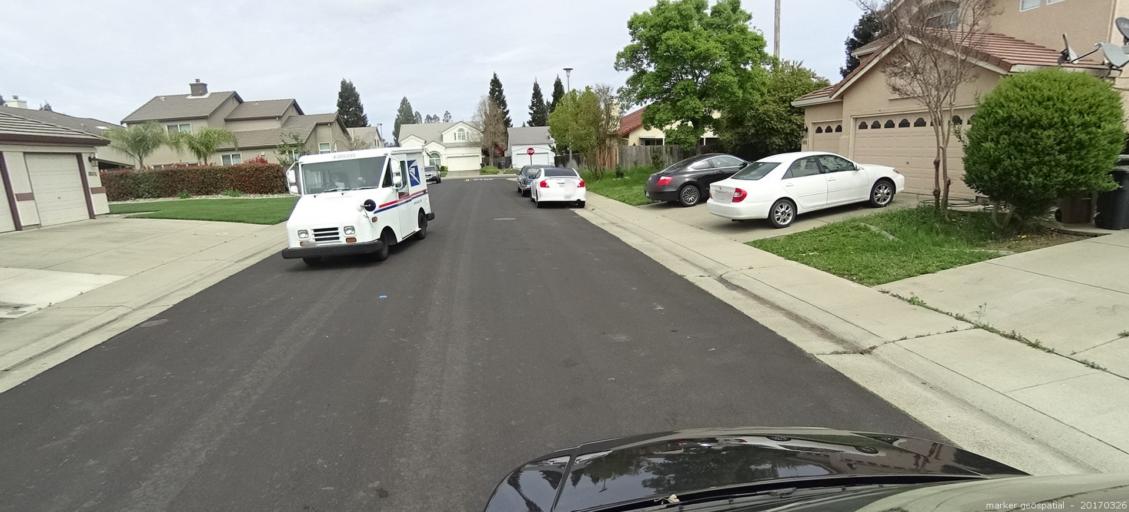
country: US
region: California
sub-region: Sacramento County
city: Laguna
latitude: 38.4376
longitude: -121.4294
